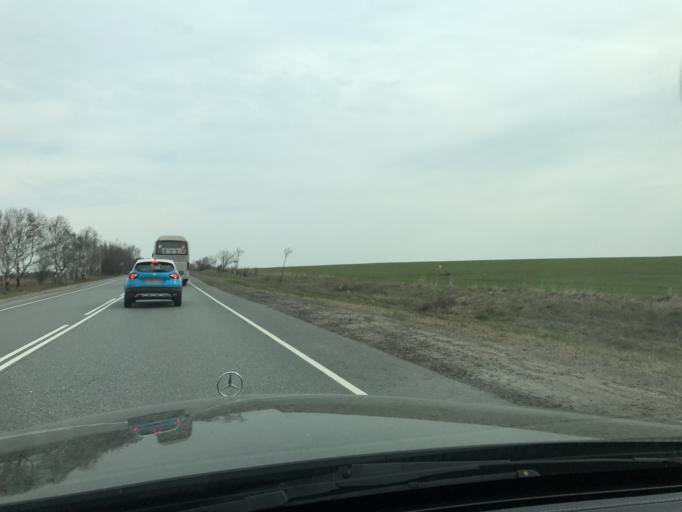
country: RU
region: Vladimir
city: Bogolyubovo
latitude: 56.2887
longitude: 40.4681
